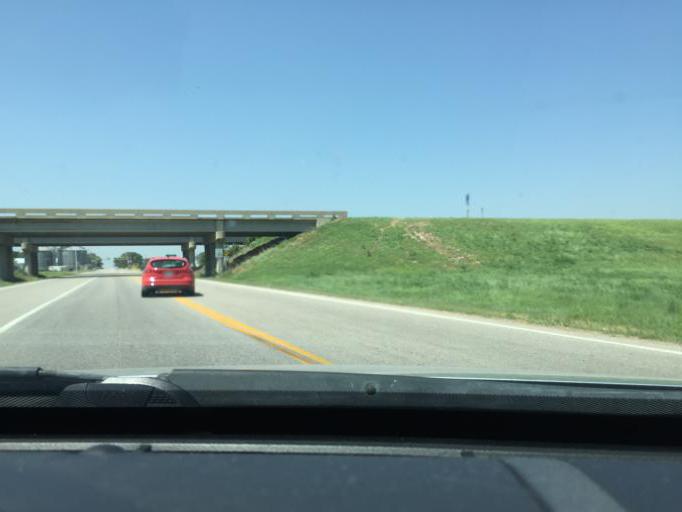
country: US
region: Kansas
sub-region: Reno County
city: Haven
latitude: 37.9353
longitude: -97.8668
